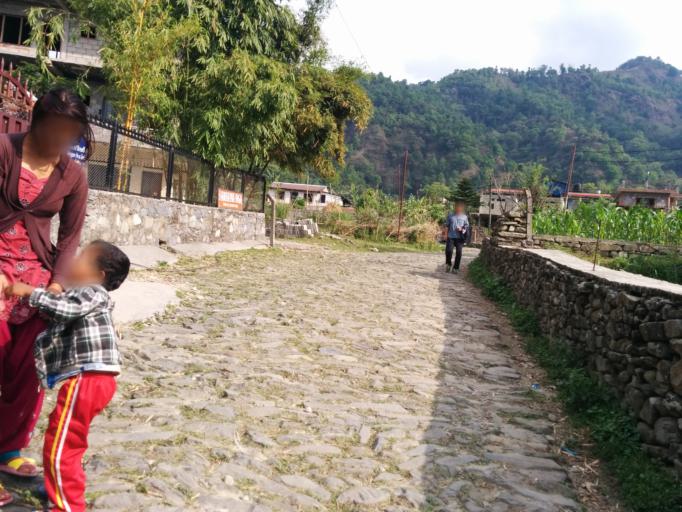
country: NP
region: Western Region
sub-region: Gandaki Zone
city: Pokhara
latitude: 28.2271
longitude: 83.9500
